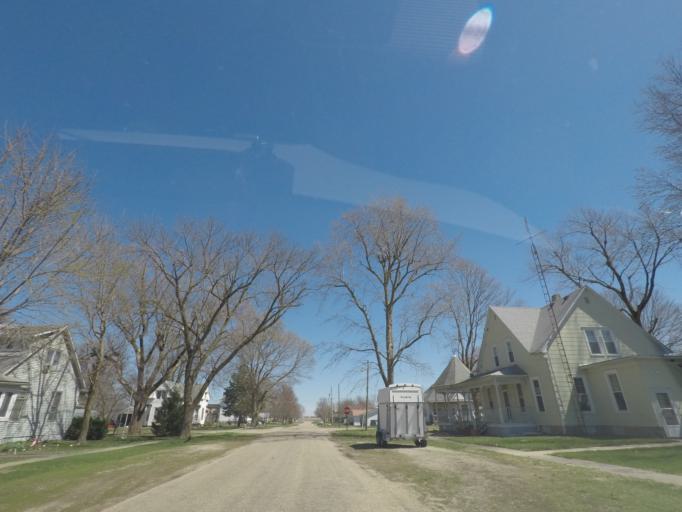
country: US
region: Illinois
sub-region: Macon County
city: Warrensburg
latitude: 39.9664
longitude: -89.1608
